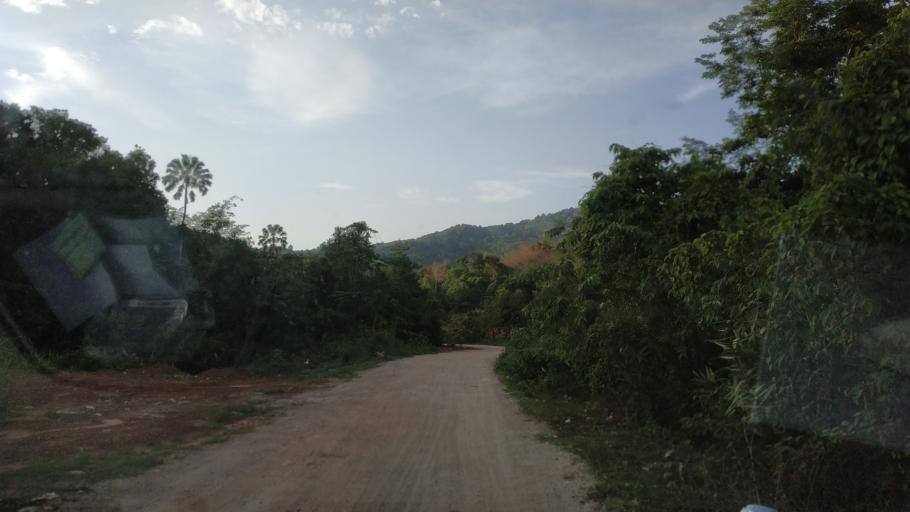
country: MM
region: Mon
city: Kyaikto
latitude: 17.4342
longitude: 97.0407
